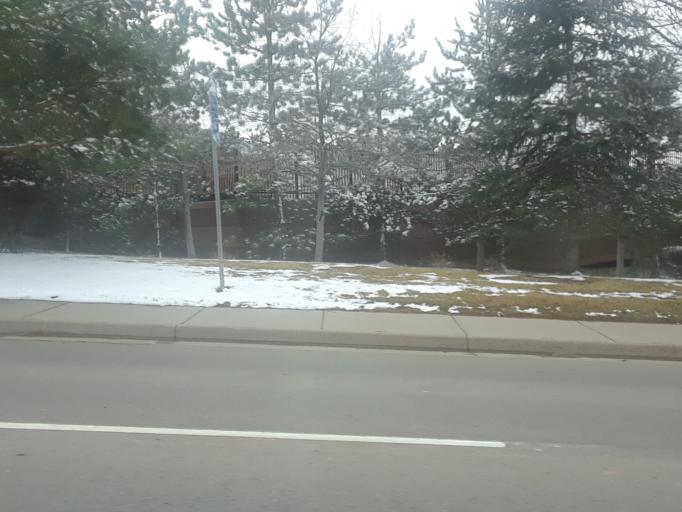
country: US
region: Colorado
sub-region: Arapahoe County
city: Centennial
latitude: 39.5747
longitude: -104.8814
